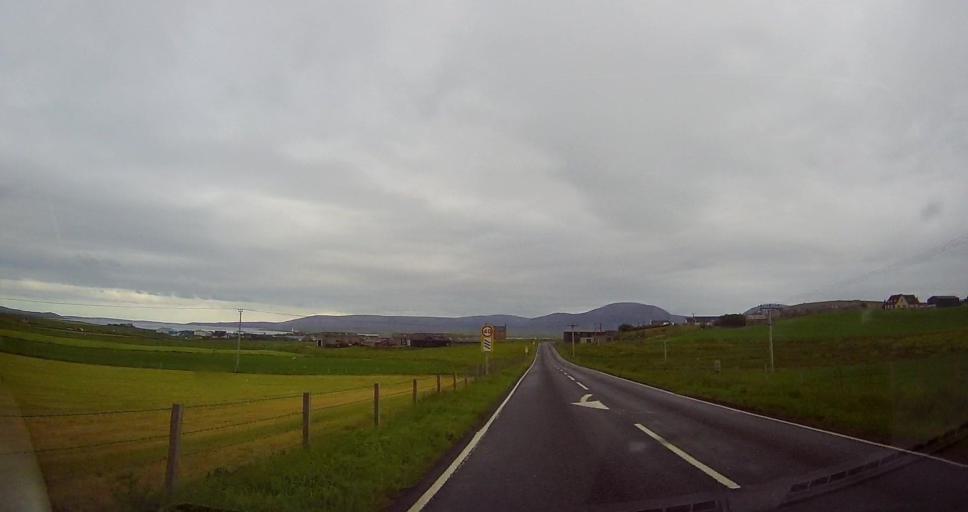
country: GB
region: Scotland
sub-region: Orkney Islands
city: Stromness
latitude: 58.9769
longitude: -3.2877
